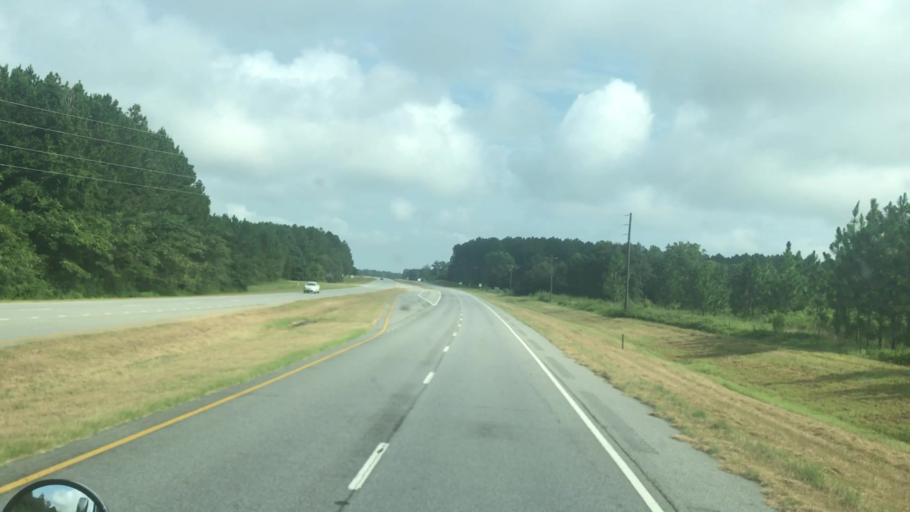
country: US
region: Georgia
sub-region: Miller County
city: Colquitt
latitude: 31.2253
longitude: -84.7804
